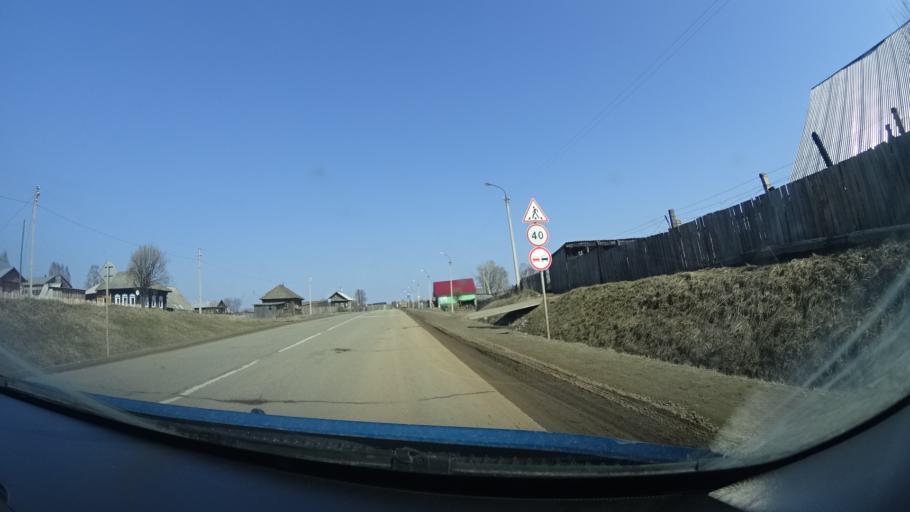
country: RU
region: Perm
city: Yugo-Kamskiy
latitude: 57.4534
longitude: 55.6578
